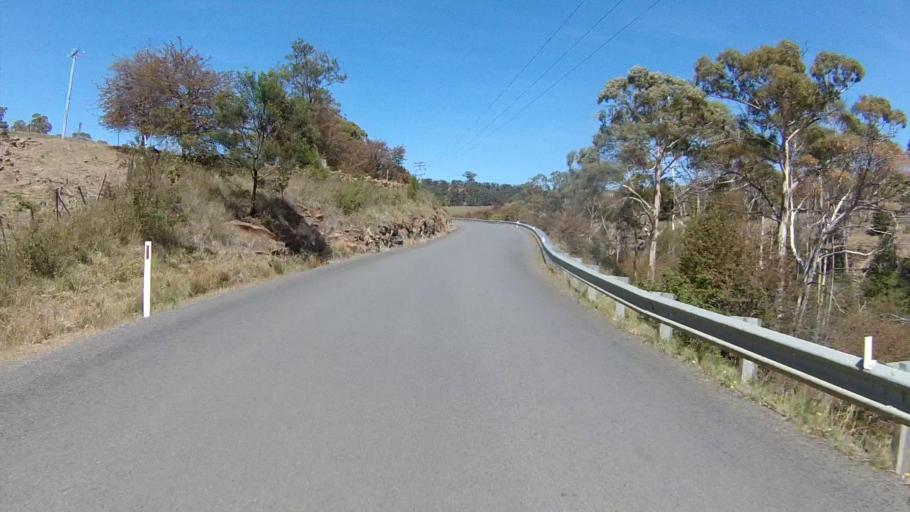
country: AU
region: Tasmania
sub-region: Sorell
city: Sorell
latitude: -42.7608
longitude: 147.6514
